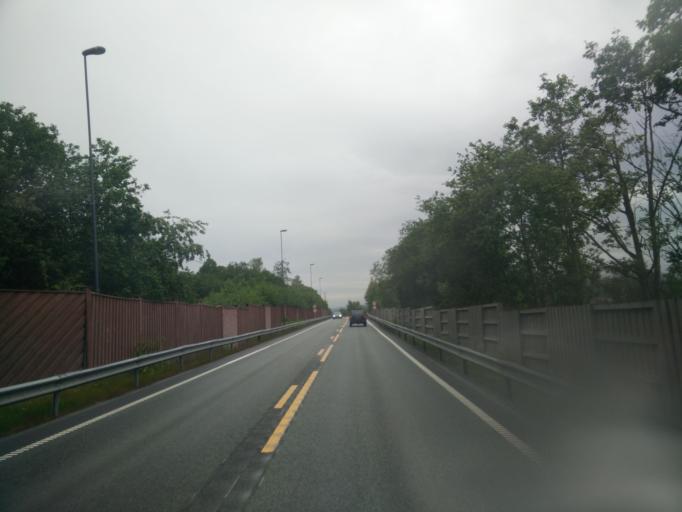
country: NO
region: Sor-Trondelag
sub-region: Orkdal
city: Orkanger
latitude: 63.3103
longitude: 9.8615
